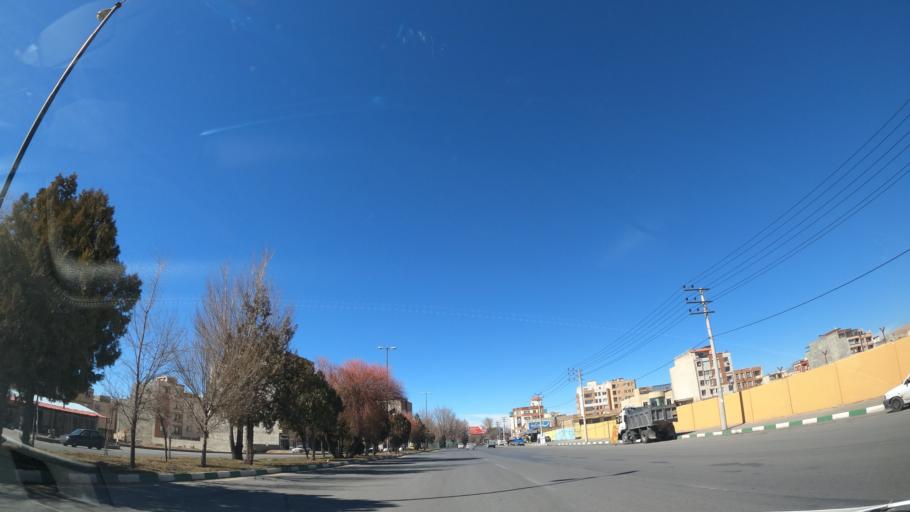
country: IR
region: Chahar Mahall va Bakhtiari
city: Shahrekord
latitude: 32.3103
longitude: 50.8904
